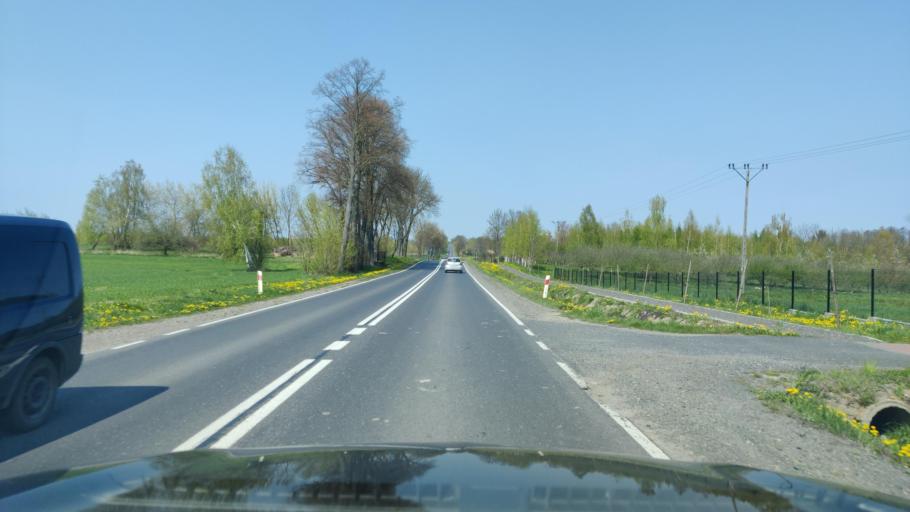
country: PL
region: Masovian Voivodeship
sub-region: Powiat pultuski
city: Pultusk
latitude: 52.6513
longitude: 21.0874
